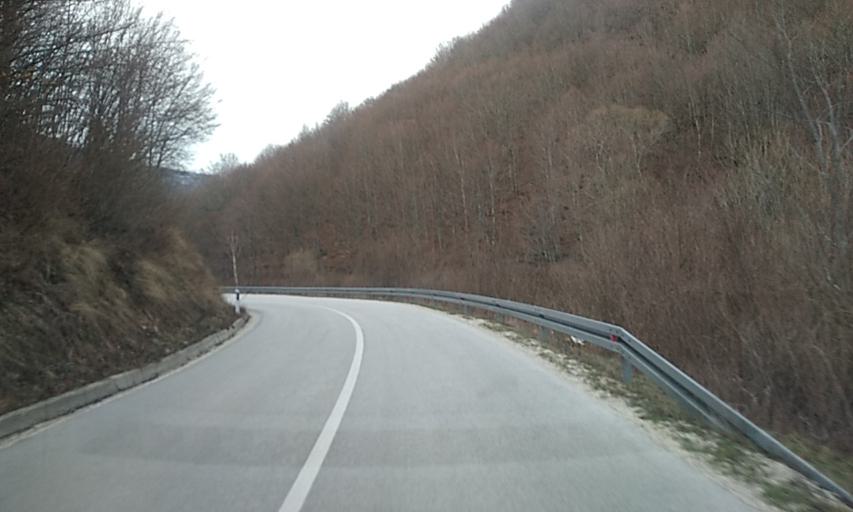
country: RS
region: Central Serbia
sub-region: Pcinjski Okrug
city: Bosilegrad
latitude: 42.5892
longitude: 22.4117
